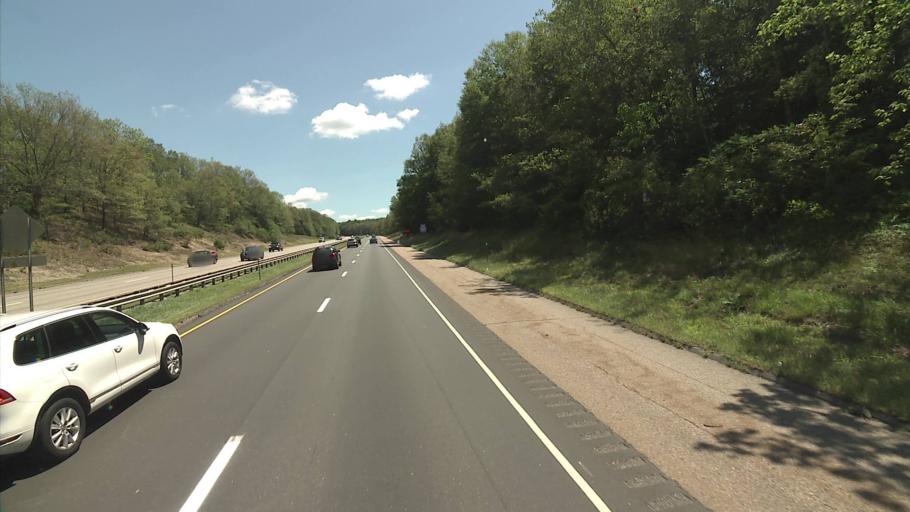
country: US
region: Connecticut
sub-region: New London County
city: Lisbon
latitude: 41.5853
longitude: -72.0429
